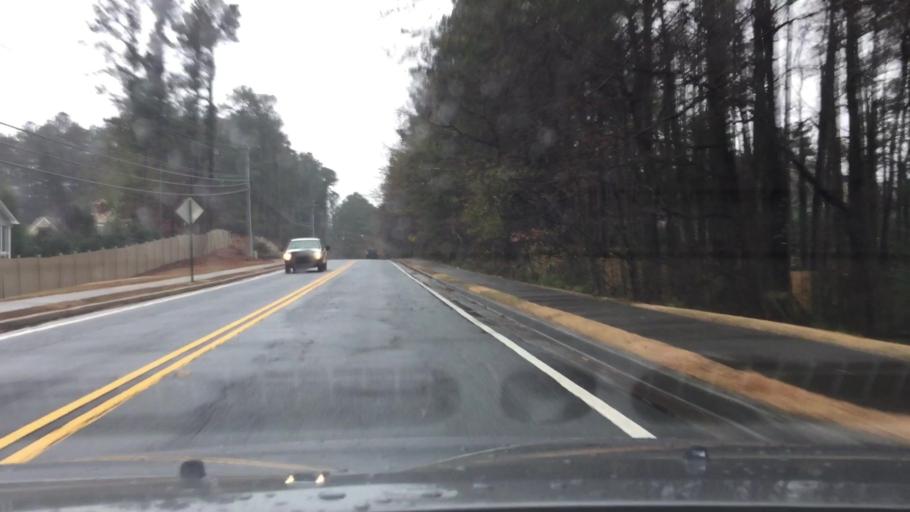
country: US
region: Georgia
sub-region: Cobb County
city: Fair Oaks
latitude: 33.9100
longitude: -84.6077
